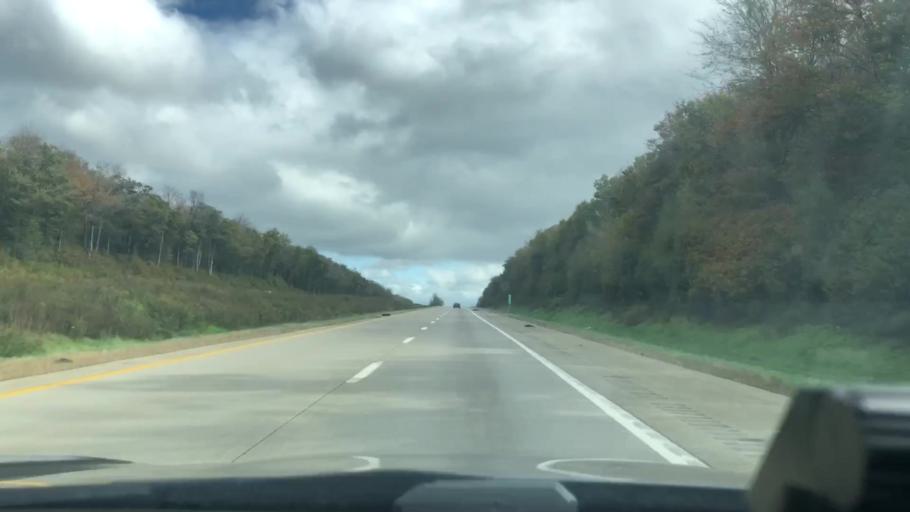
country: US
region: Pennsylvania
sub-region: Monroe County
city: Pocono Pines
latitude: 41.2146
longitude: -75.4745
